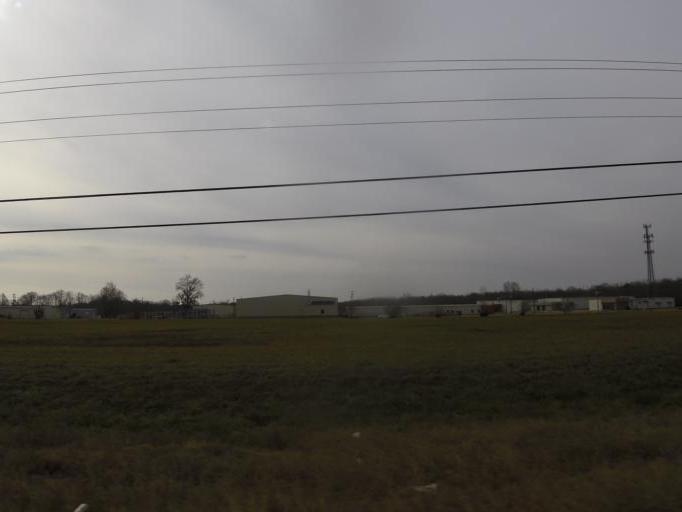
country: US
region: Alabama
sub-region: Montgomery County
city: Pike Road
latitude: 32.3029
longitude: -86.2082
